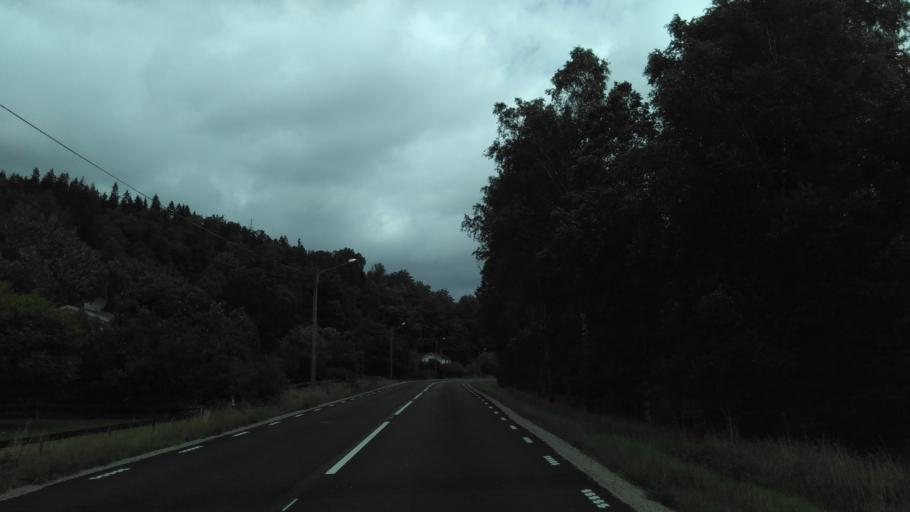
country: SE
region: Vaestra Goetaland
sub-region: Boras Kommun
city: Viskafors
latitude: 57.6097
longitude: 12.7939
